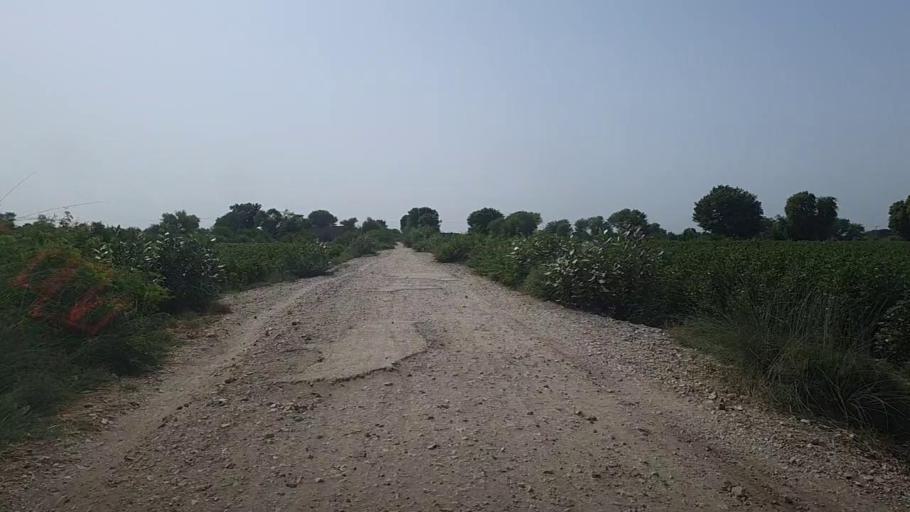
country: PK
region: Sindh
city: Pad Idan
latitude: 26.7643
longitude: 68.3292
